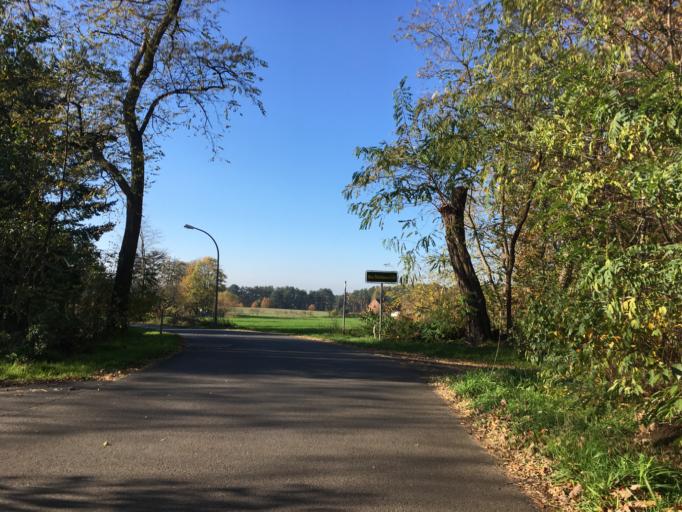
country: DE
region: Brandenburg
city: Reichenwalde
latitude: 52.2895
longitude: 14.0160
